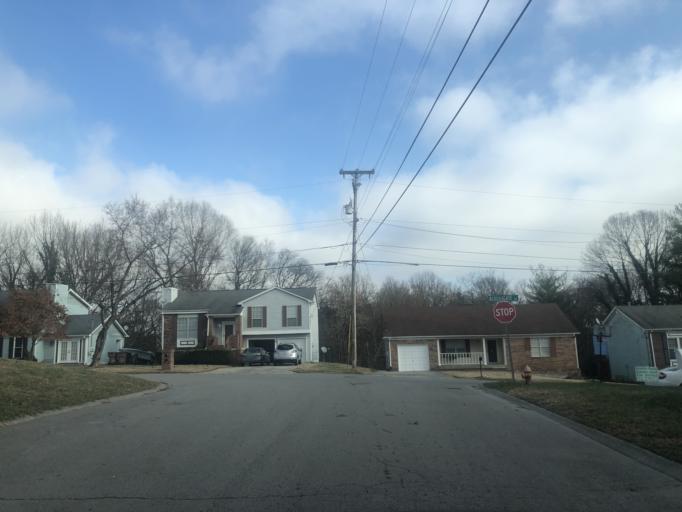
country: US
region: Tennessee
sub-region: Rutherford County
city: La Vergne
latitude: 36.0829
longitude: -86.6585
